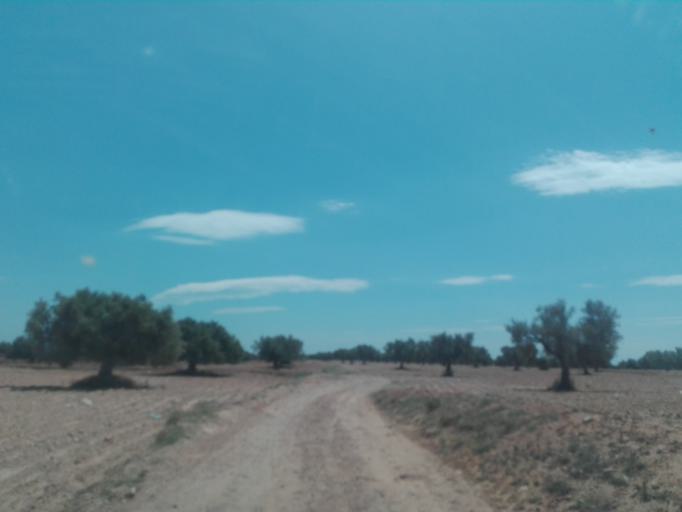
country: TN
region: Safaqis
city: Sfax
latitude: 34.6528
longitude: 10.5902
